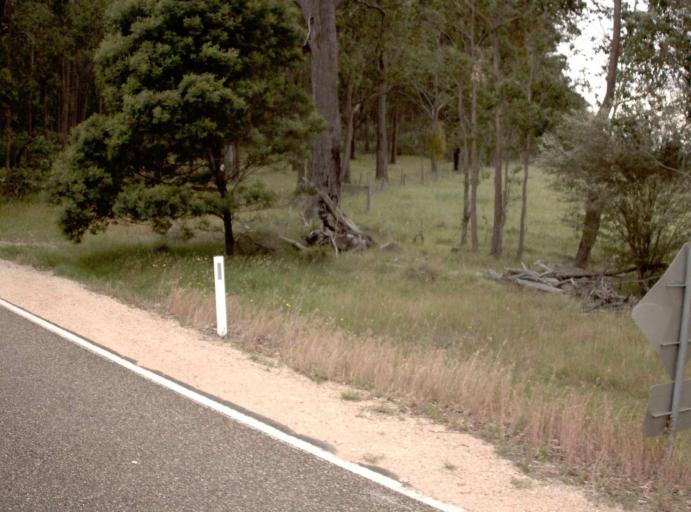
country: AU
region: Victoria
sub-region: East Gippsland
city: Bairnsdale
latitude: -37.7545
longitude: 147.3222
